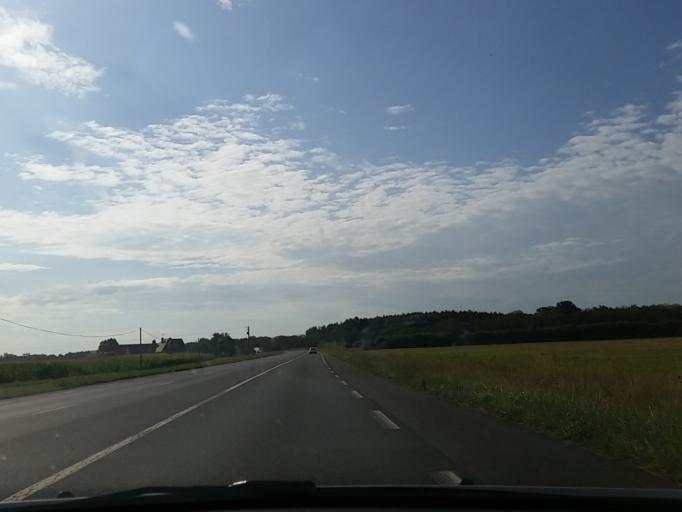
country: FR
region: Centre
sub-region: Departement du Loir-et-Cher
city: Soings-en-Sologne
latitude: 47.4433
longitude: 1.5437
